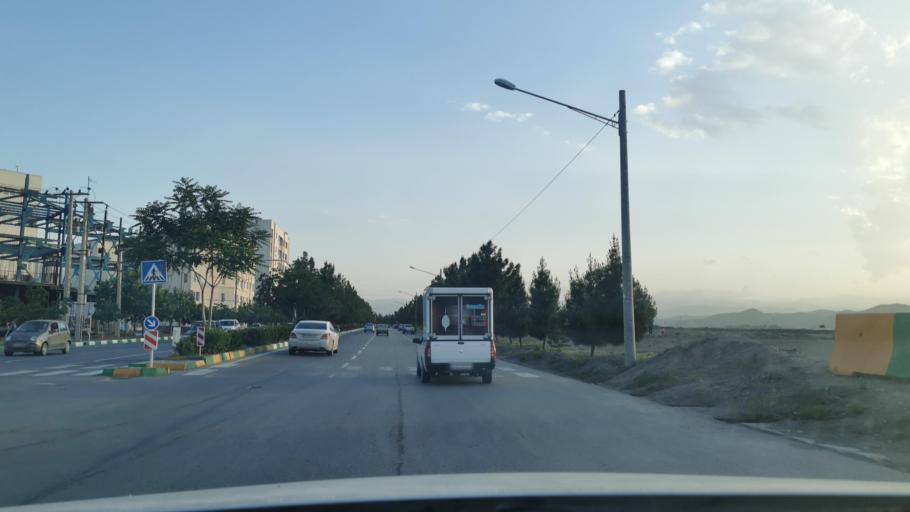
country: IR
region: Razavi Khorasan
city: Mashhad
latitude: 36.3906
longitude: 59.4695
